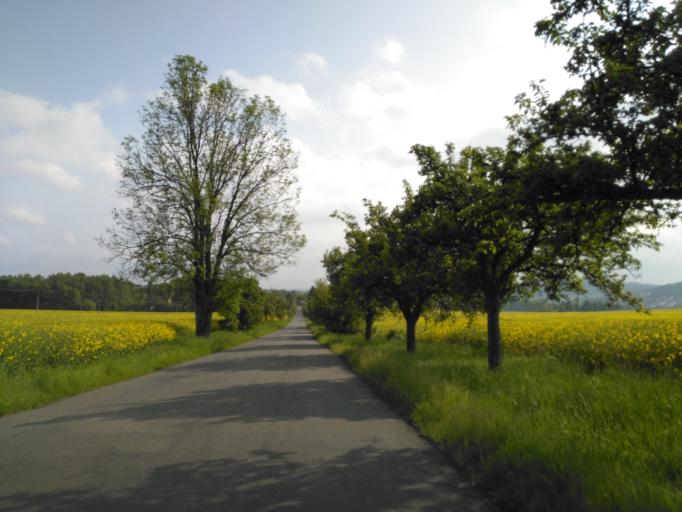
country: CZ
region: Plzensky
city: Zbiroh
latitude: 49.8762
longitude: 13.7978
